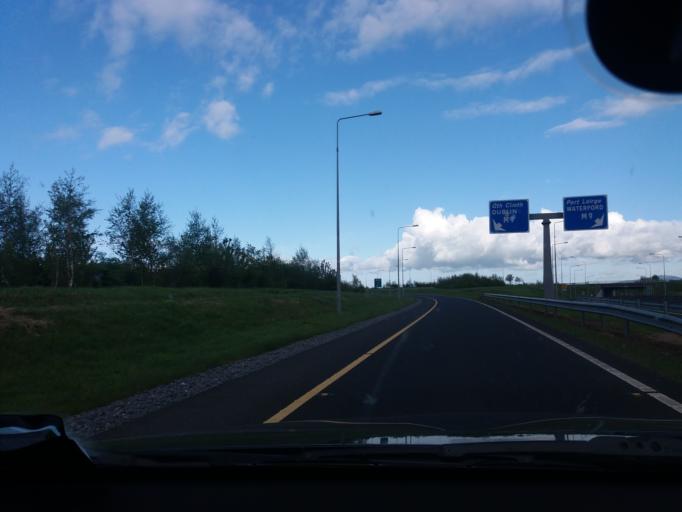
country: IE
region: Leinster
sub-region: Kilkenny
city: Kilkenny
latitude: 52.6347
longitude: -7.1505
